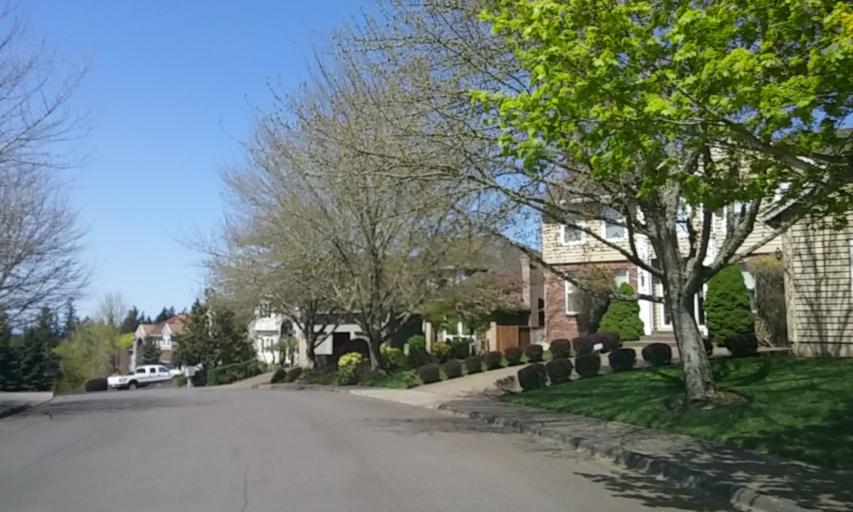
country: US
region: Oregon
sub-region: Washington County
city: West Haven
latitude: 45.5225
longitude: -122.7705
